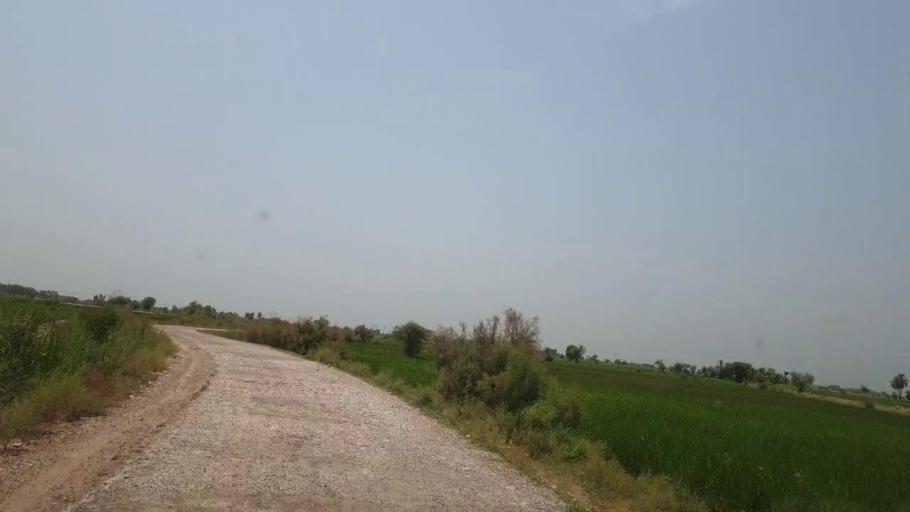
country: PK
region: Sindh
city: Shikarpur
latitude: 27.9016
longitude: 68.6325
